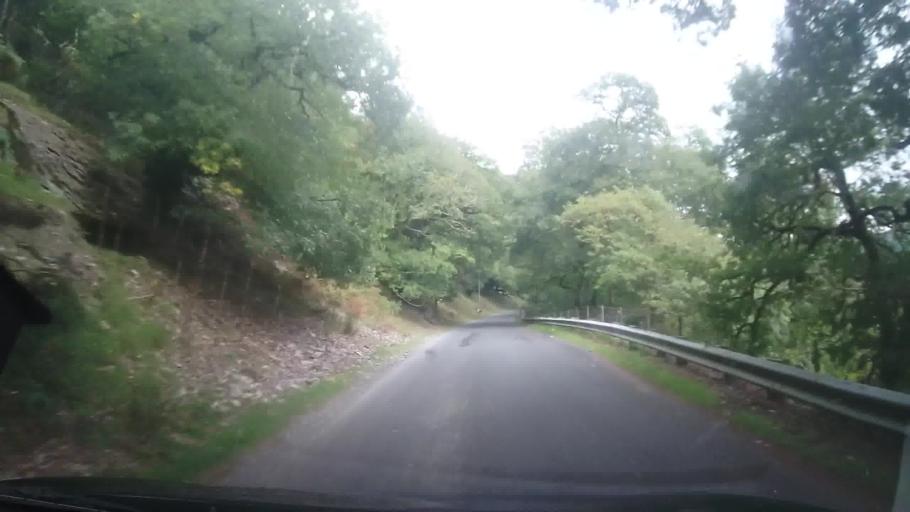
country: GB
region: Wales
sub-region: Sir Powys
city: Rhayader
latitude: 52.3144
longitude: -3.5504
